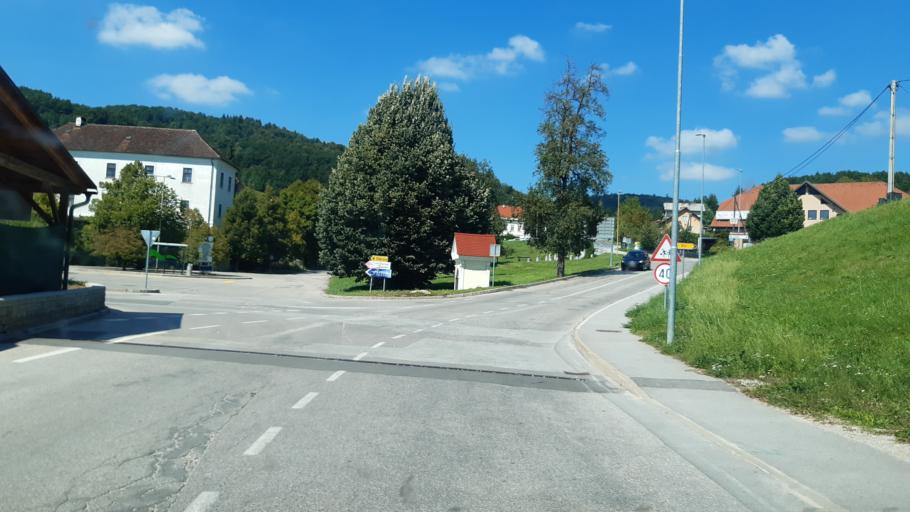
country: SI
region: Ivancna Gorica
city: Ivancna Gorica
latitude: 45.9555
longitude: 14.8065
